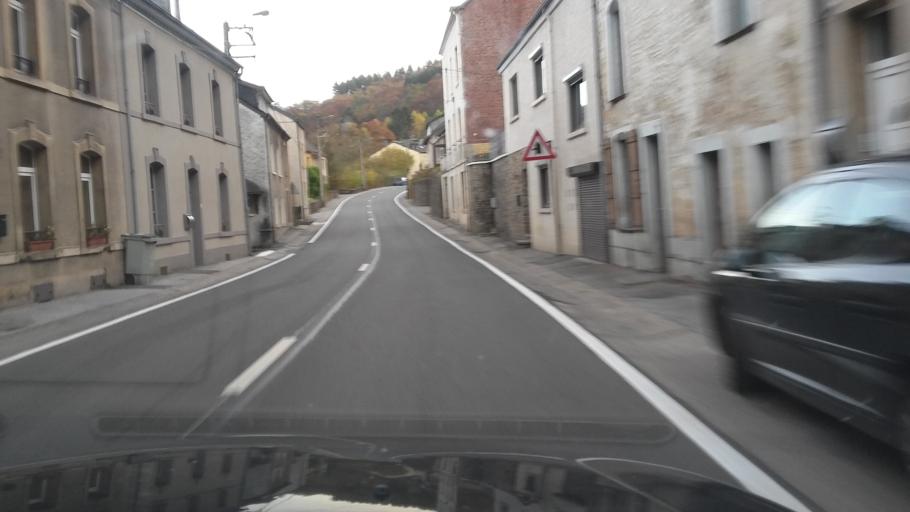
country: BE
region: Wallonia
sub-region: Province du Luxembourg
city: Bouillon
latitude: 49.7892
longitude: 5.0647
